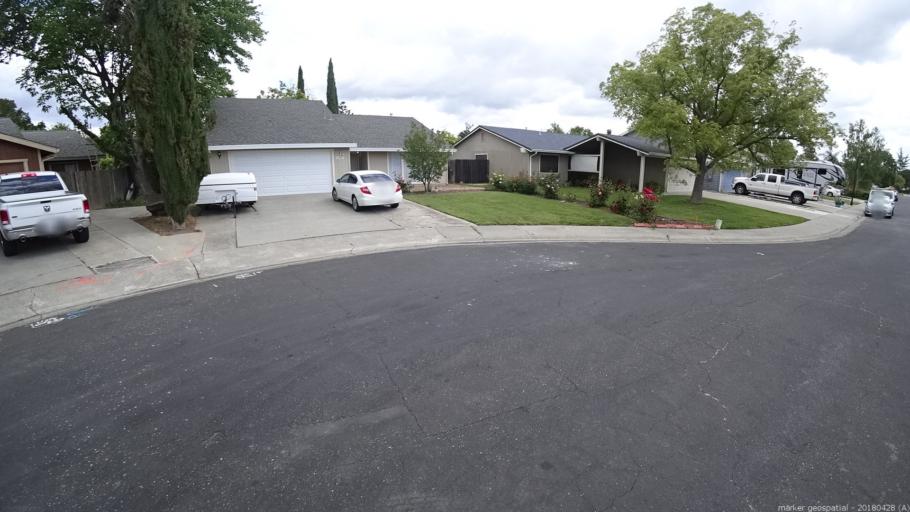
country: US
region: California
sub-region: Yolo County
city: West Sacramento
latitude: 38.5487
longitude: -121.5581
